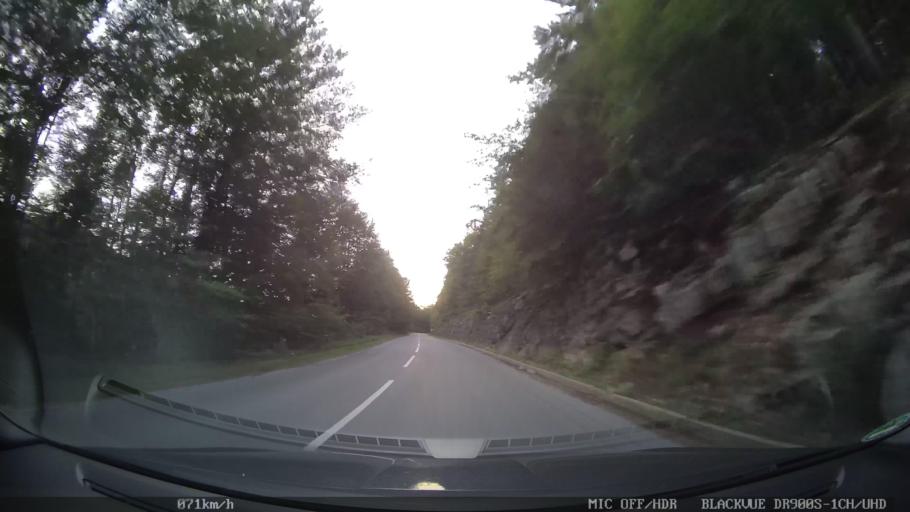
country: HR
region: Primorsko-Goranska
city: Novi Vinodolski
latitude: 45.1656
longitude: 14.9354
